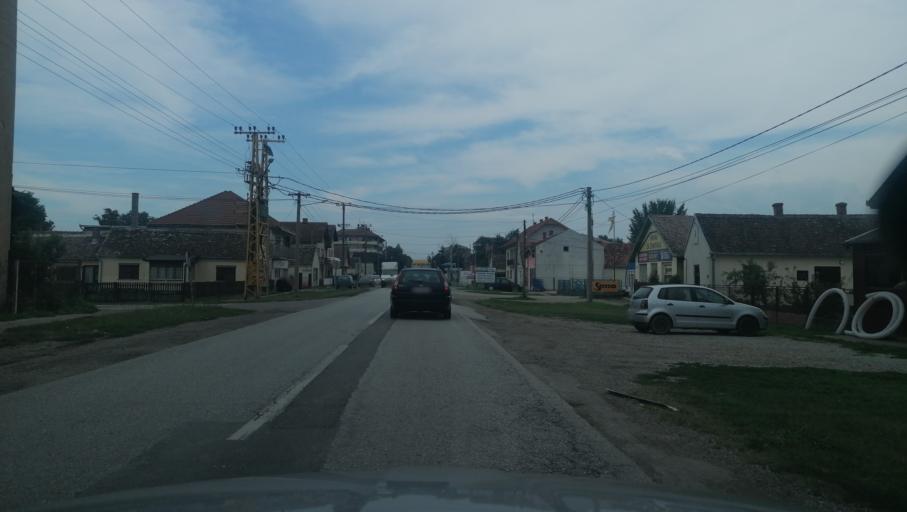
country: RS
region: Central Serbia
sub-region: Macvanski Okrug
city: Bogatic
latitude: 44.8344
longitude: 19.4754
